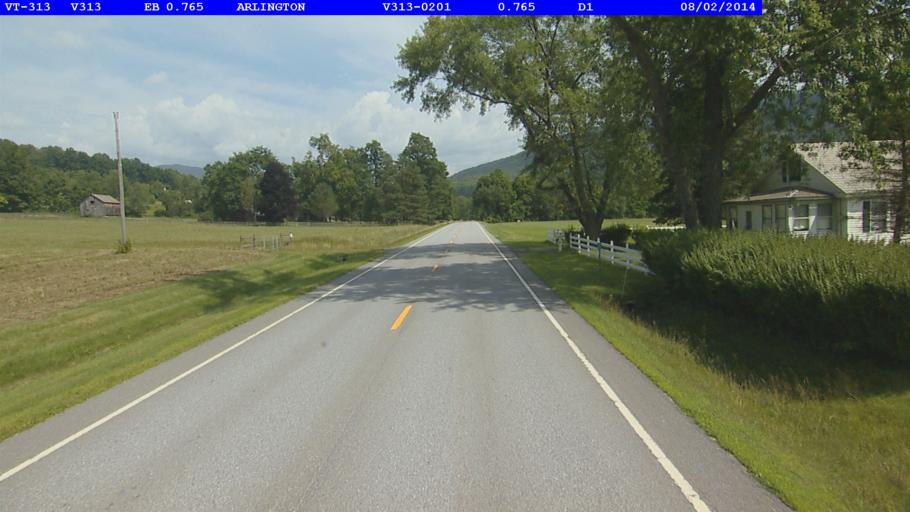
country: US
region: Vermont
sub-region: Bennington County
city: Arlington
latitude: 43.1035
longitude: -73.2512
